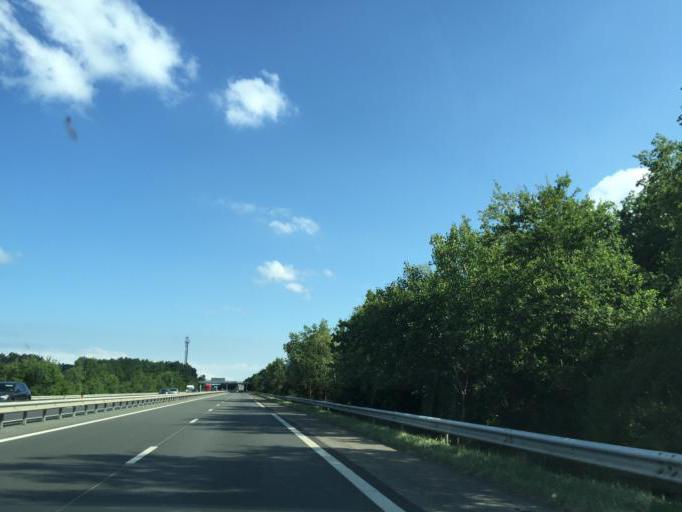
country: FR
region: Rhone-Alpes
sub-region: Departement de la Loire
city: Balbigny
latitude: 45.7870
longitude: 4.1393
